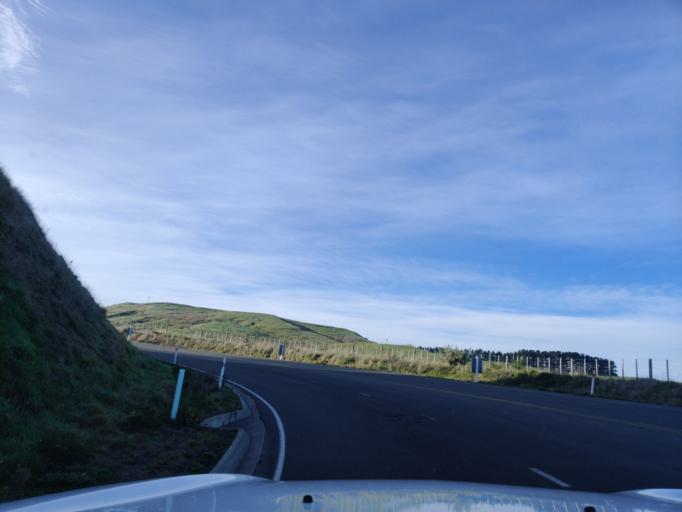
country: NZ
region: Manawatu-Wanganui
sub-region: Palmerston North City
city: Palmerston North
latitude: -40.2858
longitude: 175.7717
